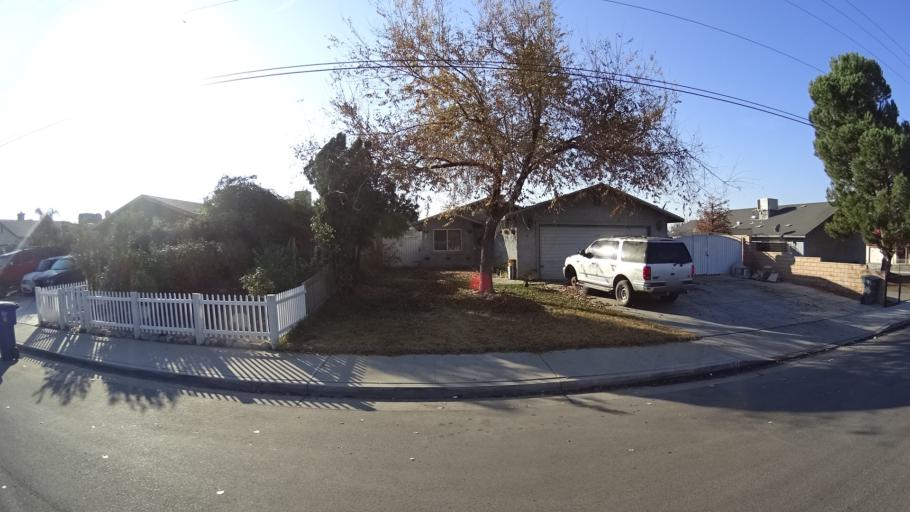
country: US
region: California
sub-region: Kern County
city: Greenfield
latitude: 35.3031
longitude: -119.0082
